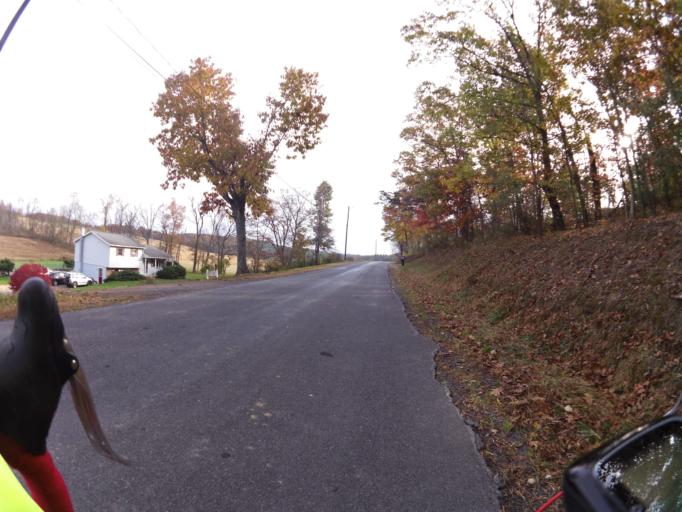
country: US
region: Pennsylvania
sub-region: Union County
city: New Columbia
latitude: 41.0281
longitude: -76.9303
